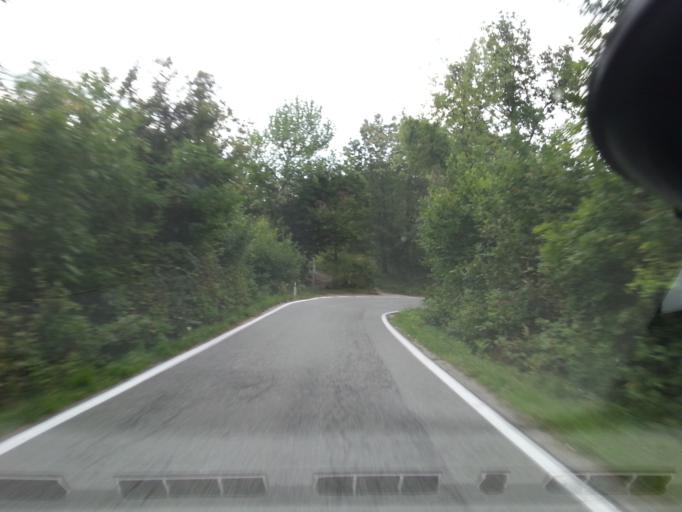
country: IT
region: Piedmont
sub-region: Provincia di Torino
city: Valgioie
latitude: 45.0689
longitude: 7.3695
